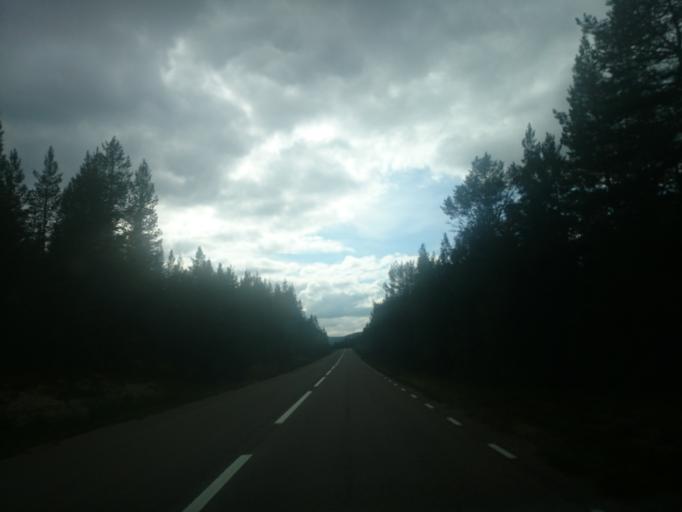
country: SE
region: Jaemtland
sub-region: Harjedalens Kommun
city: Sveg
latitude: 62.3480
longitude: 13.7807
